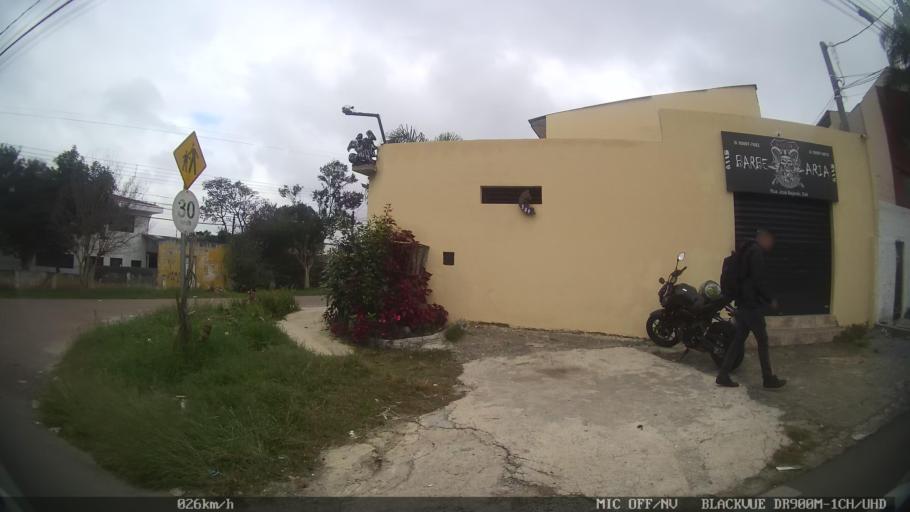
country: BR
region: Parana
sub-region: Almirante Tamandare
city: Almirante Tamandare
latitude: -25.3673
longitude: -49.2732
